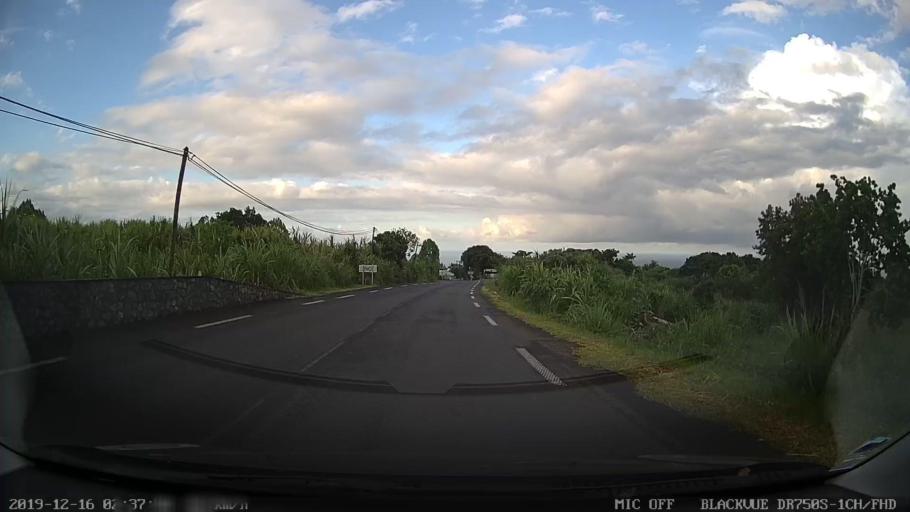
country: RE
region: Reunion
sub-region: Reunion
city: Saint-Benoit
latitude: -21.0870
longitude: 55.6908
